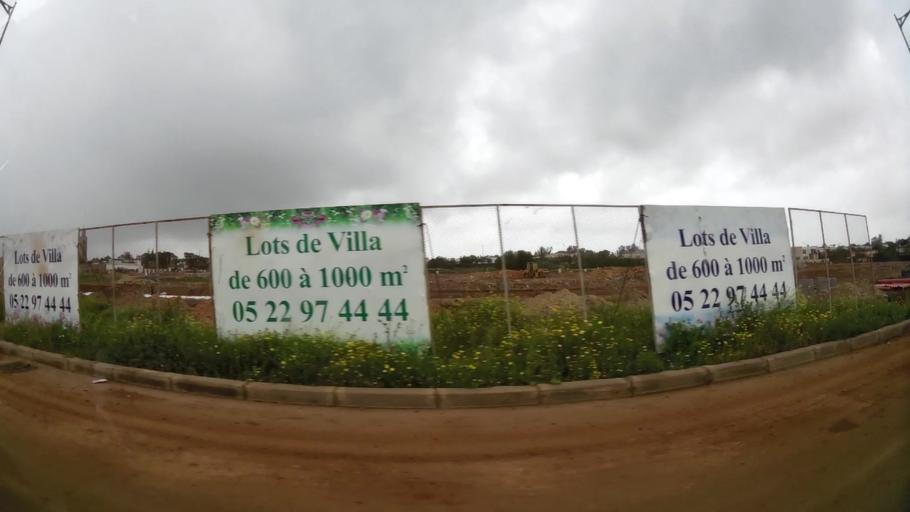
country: MA
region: Grand Casablanca
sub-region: Casablanca
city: Casablanca
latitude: 33.5226
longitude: -7.6271
